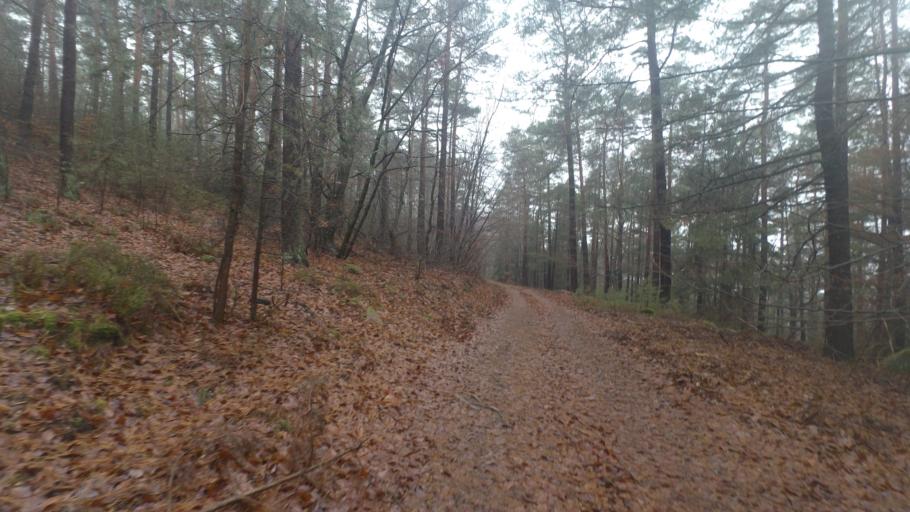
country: DE
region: Rheinland-Pfalz
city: Lindenberg
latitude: 49.3985
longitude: 8.1328
